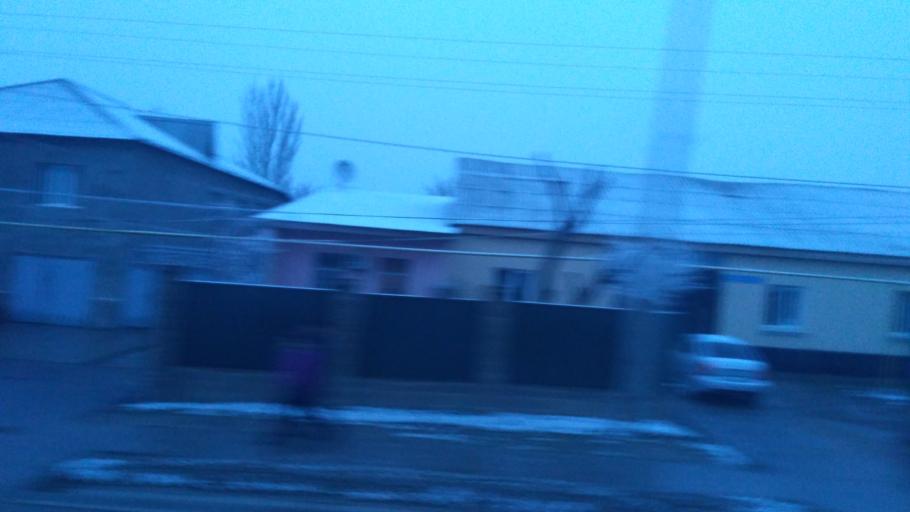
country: KZ
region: Ongtustik Qazaqstan
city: Shymkent
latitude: 42.3702
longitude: 69.5074
